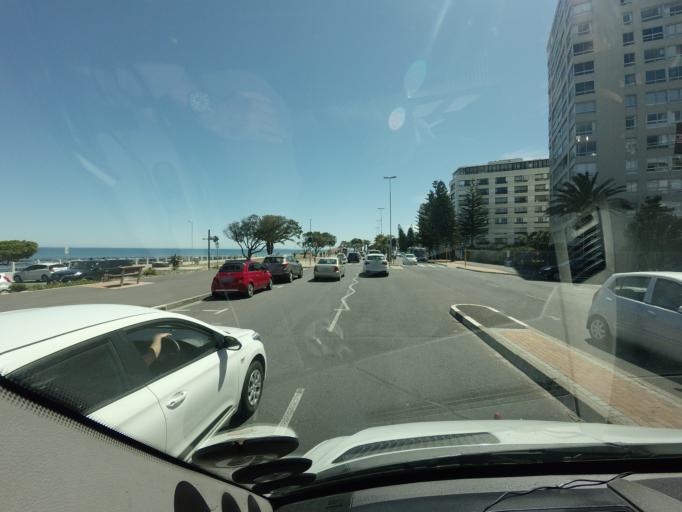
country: ZA
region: Western Cape
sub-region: City of Cape Town
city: Cape Town
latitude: -33.9168
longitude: 18.3864
